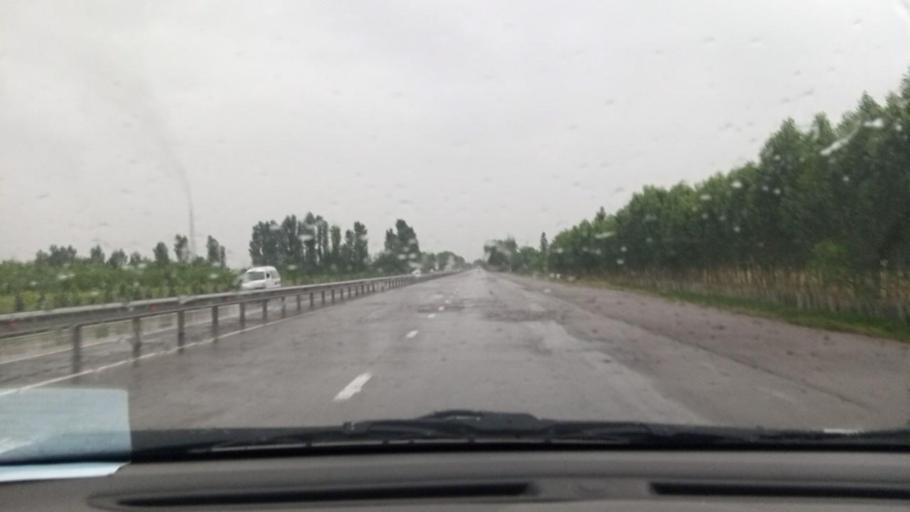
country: UZ
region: Toshkent
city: Ohangaron
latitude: 40.9088
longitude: 69.7821
